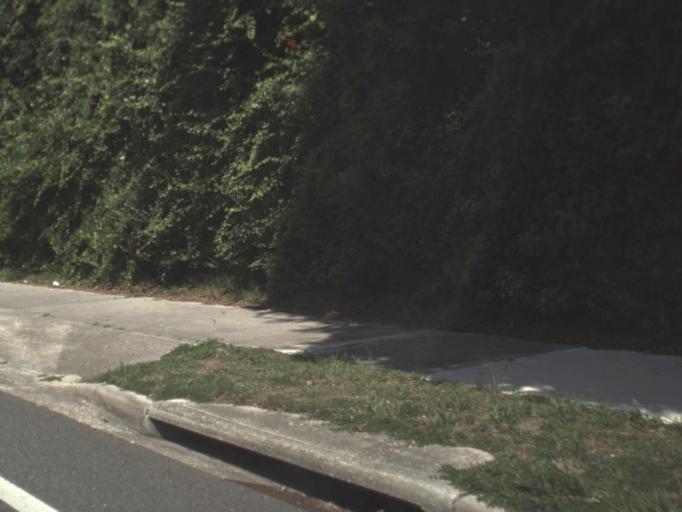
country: US
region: Florida
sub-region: Alachua County
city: Gainesville
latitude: 29.6118
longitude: -82.3597
